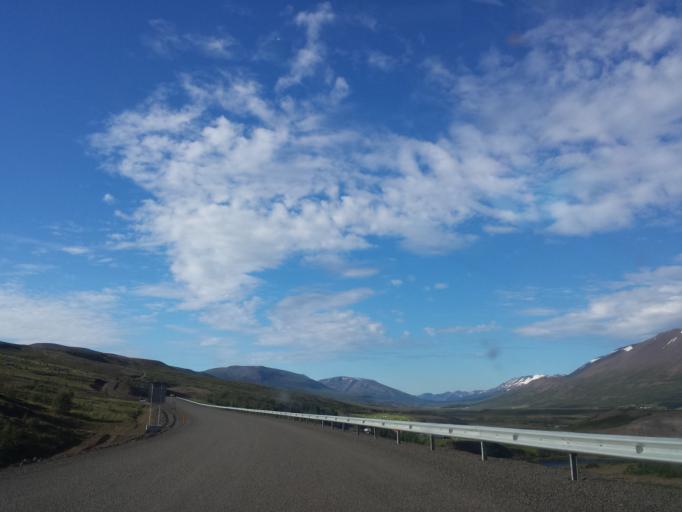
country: IS
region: Northeast
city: Akureyri
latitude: 65.7310
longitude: -17.9177
